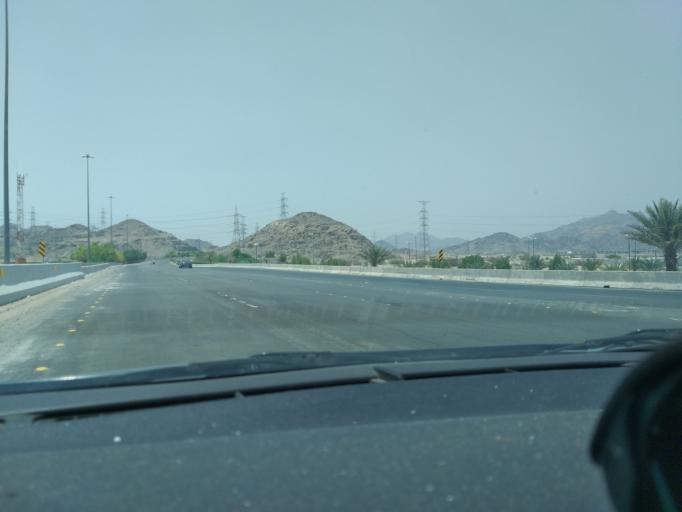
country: SA
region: Makkah
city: Mecca
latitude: 21.3361
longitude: 39.9473
